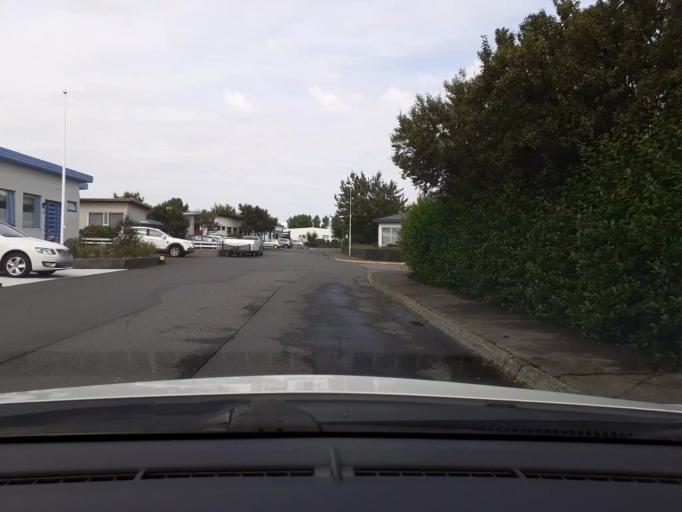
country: IS
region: Southern Peninsula
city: Reykjanesbaer
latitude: 63.9875
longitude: -22.5573
